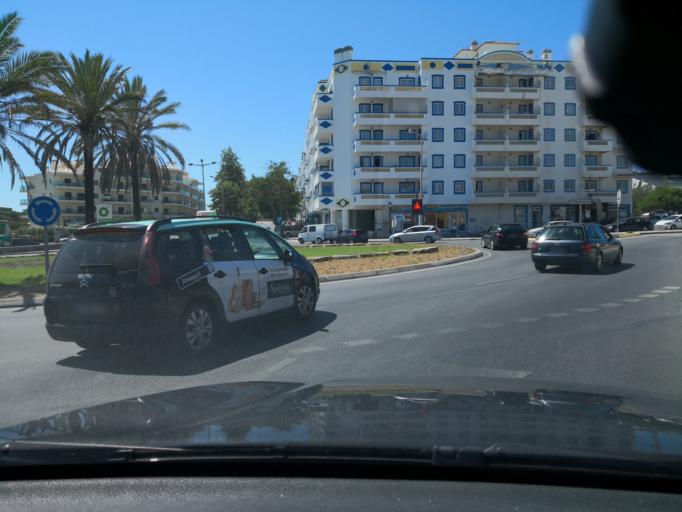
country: PT
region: Faro
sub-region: Loule
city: Quarteira
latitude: 37.0767
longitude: -8.0962
